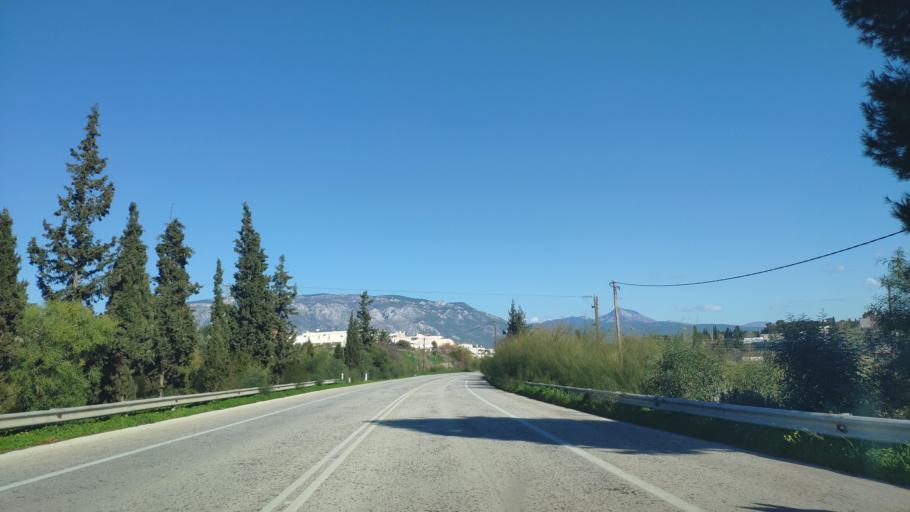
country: GR
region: Peloponnese
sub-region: Nomos Korinthias
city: Korinthos
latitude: 37.9292
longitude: 22.9206
